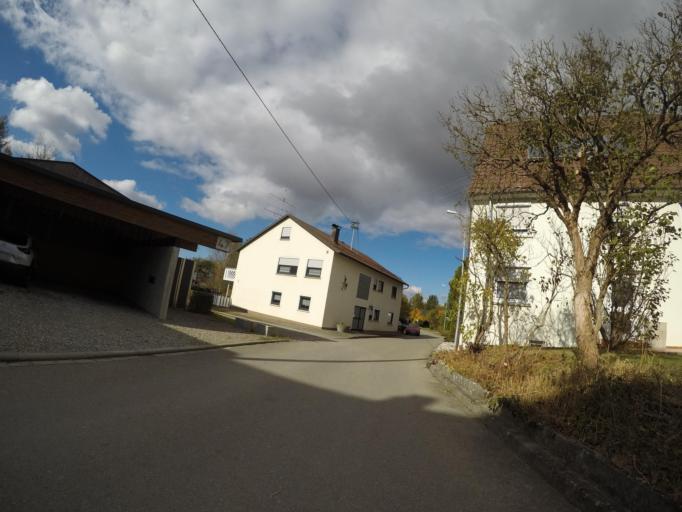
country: DE
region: Baden-Wuerttemberg
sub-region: Tuebingen Region
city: Oggelshausen
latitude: 48.0741
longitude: 9.6457
